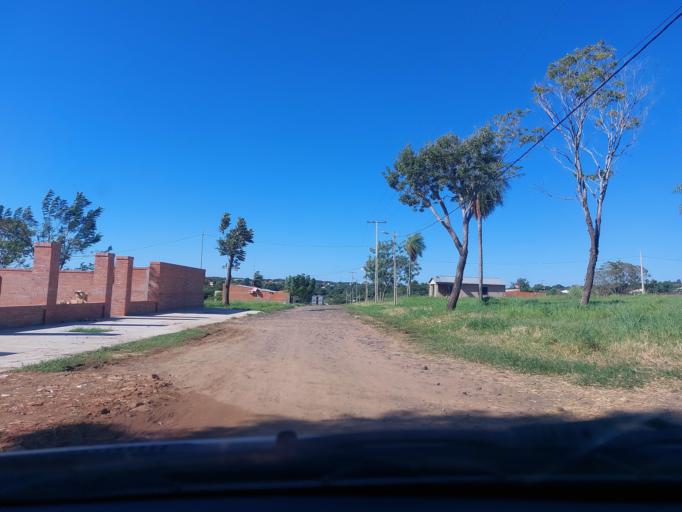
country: PY
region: San Pedro
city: Guayaybi
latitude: -24.6525
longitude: -56.4492
